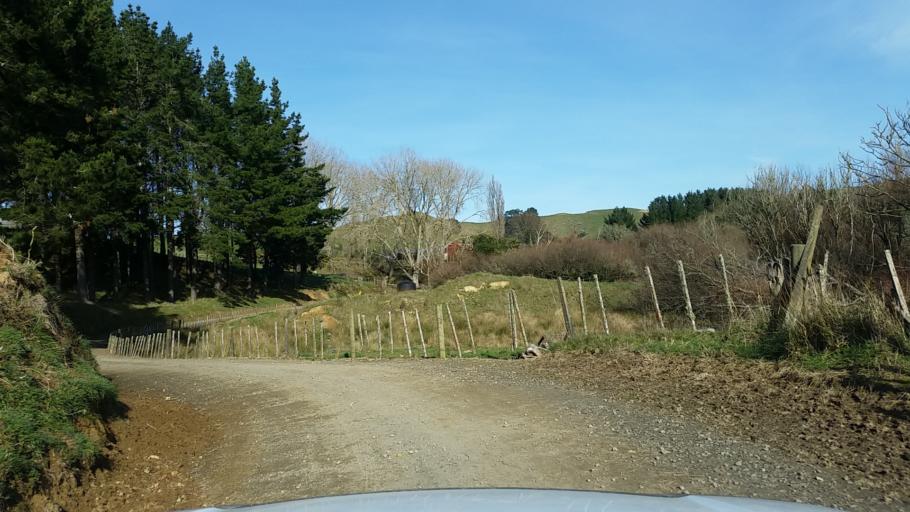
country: NZ
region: Taranaki
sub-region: South Taranaki District
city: Eltham
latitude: -39.3177
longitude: 174.5329
